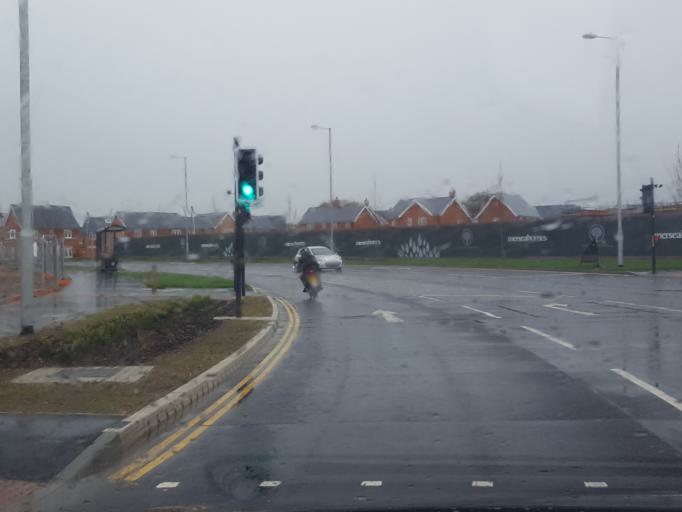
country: GB
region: England
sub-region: Essex
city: Great Horkesley
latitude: 51.9179
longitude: 0.8876
